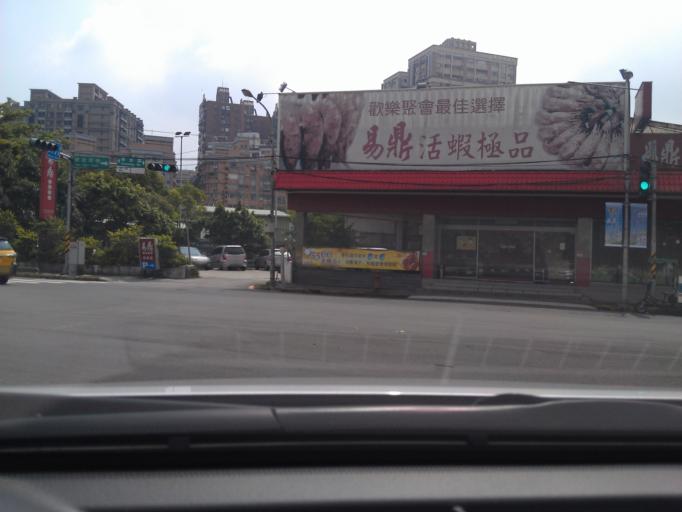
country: TW
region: Taipei
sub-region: Taipei
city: Banqiao
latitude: 25.0118
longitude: 121.5049
